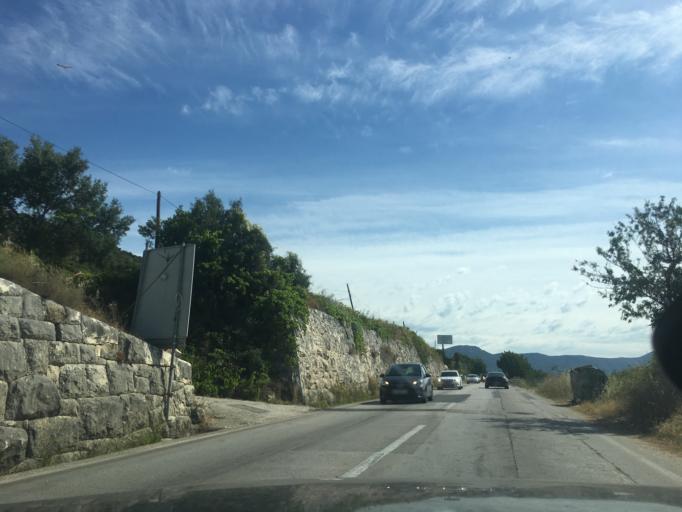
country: HR
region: Splitsko-Dalmatinska
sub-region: Grad Trogir
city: Trogir
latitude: 43.5265
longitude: 16.2706
